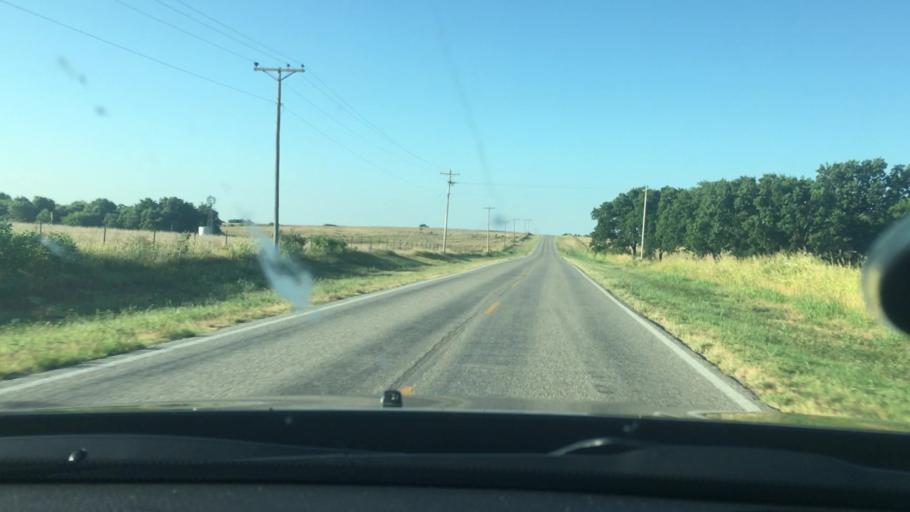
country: US
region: Oklahoma
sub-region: Murray County
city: Sulphur
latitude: 34.5888
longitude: -96.8449
